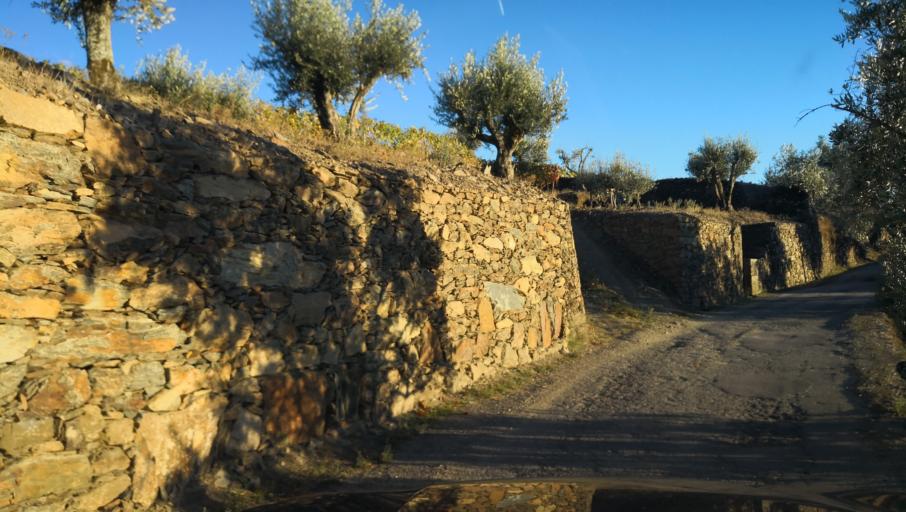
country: PT
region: Vila Real
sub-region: Santa Marta de Penaguiao
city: Santa Marta de Penaguiao
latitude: 41.2488
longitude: -7.7673
